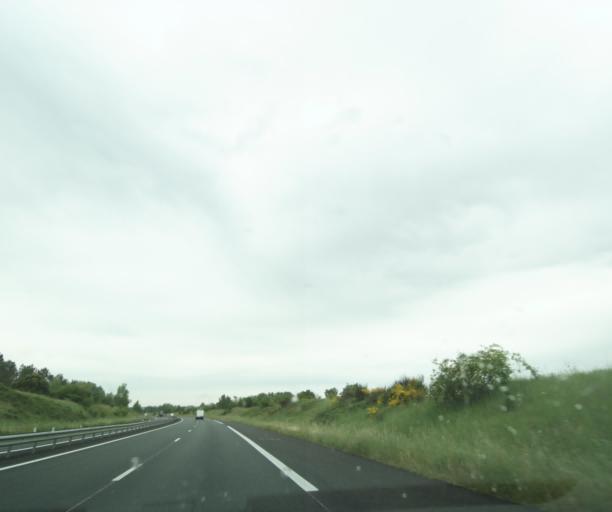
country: FR
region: Midi-Pyrenees
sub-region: Departement du Tarn-et-Garonne
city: Albias
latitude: 44.0604
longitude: 1.4219
